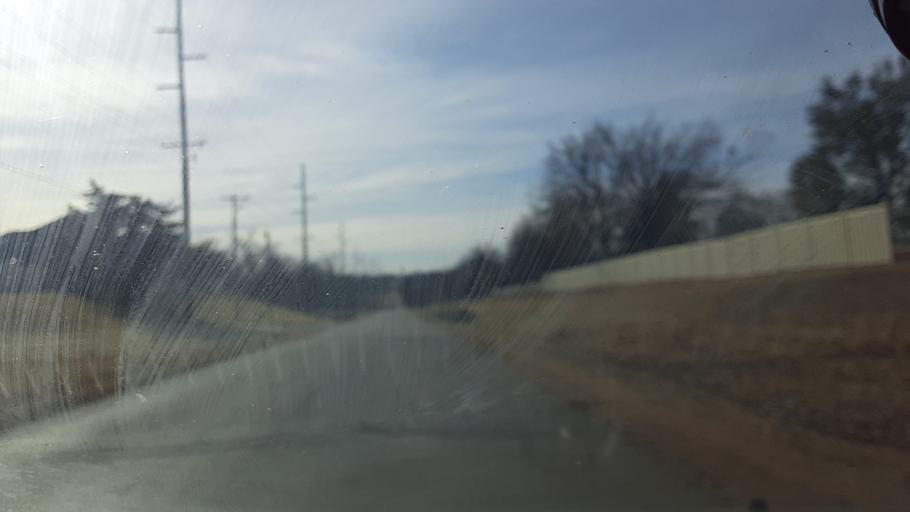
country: US
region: Oklahoma
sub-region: Logan County
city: Guthrie
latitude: 35.8911
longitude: -97.4075
